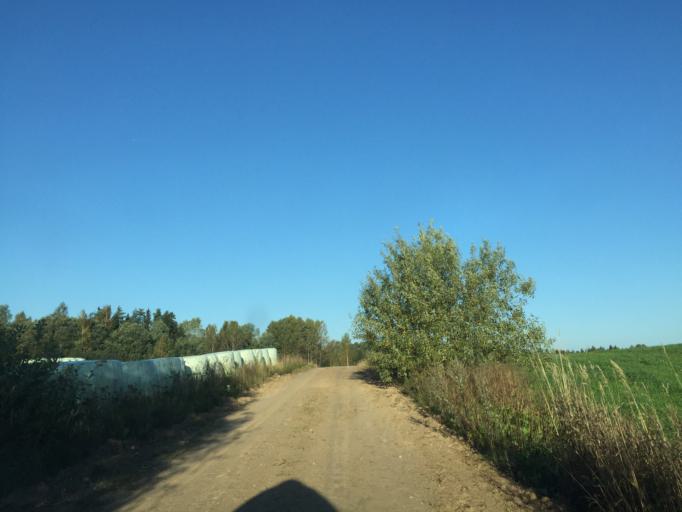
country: LV
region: Vecpiebalga
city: Vecpiebalga
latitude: 57.0637
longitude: 25.7537
